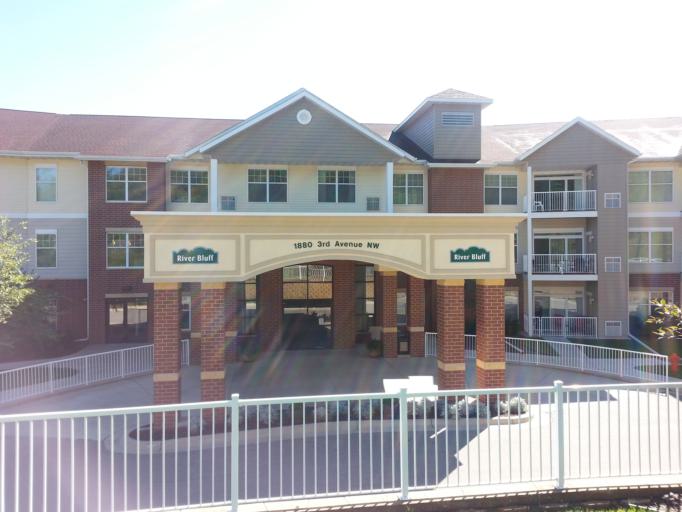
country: US
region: Minnesota
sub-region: Olmsted County
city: Rochester
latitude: 44.0427
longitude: -92.4666
